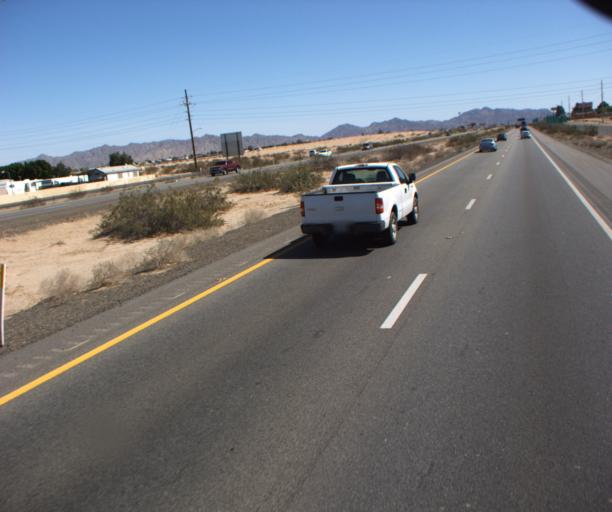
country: US
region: Arizona
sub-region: Yuma County
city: Fortuna Foothills
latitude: 32.6704
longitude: -114.4709
